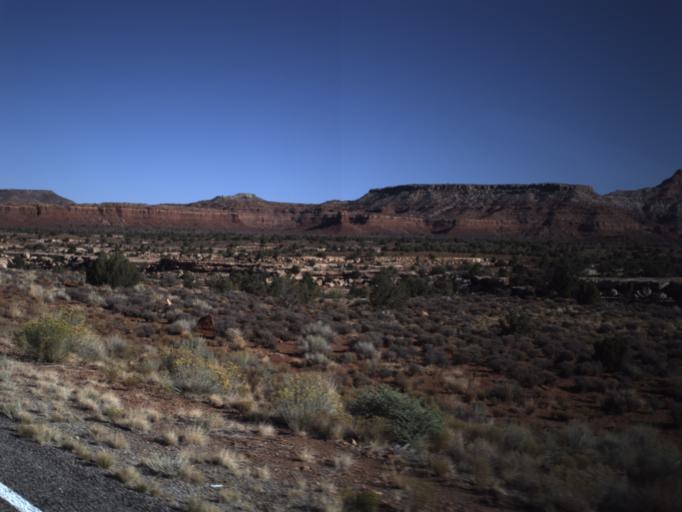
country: US
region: Utah
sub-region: San Juan County
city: Blanding
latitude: 37.6889
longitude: -110.2240
